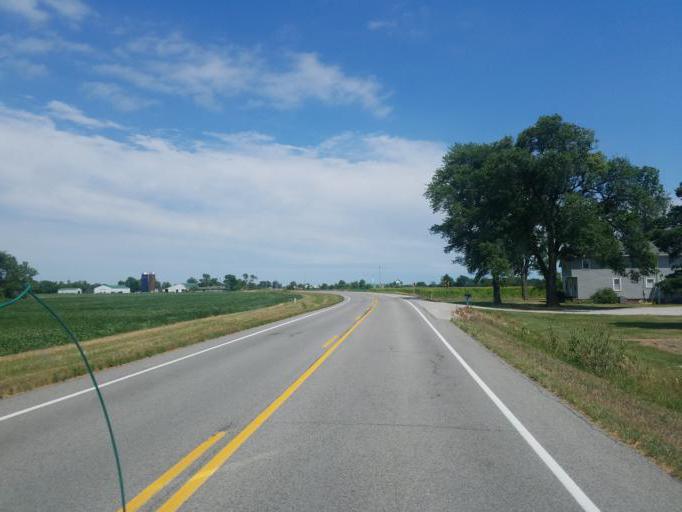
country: US
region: Indiana
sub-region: Allen County
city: Woodburn
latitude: 41.1545
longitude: -84.8367
